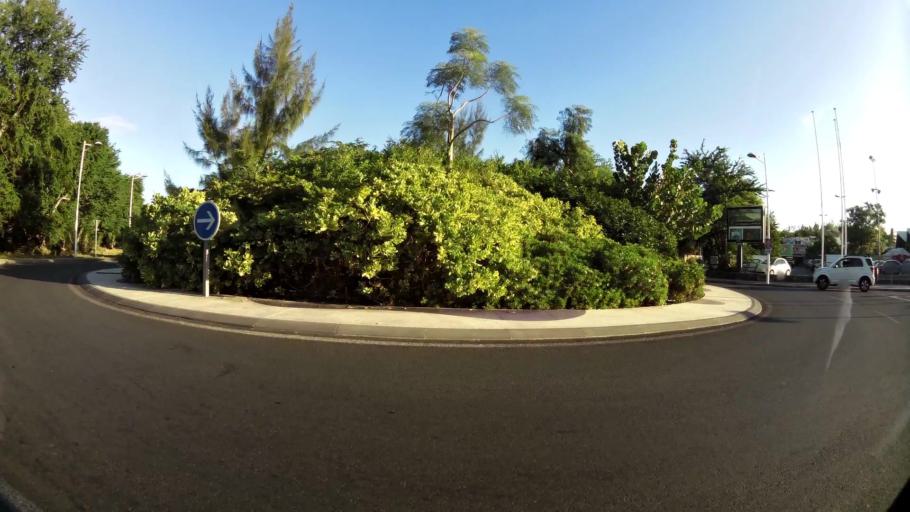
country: RE
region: Reunion
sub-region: Reunion
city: Trois-Bassins
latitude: -21.0848
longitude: 55.2322
